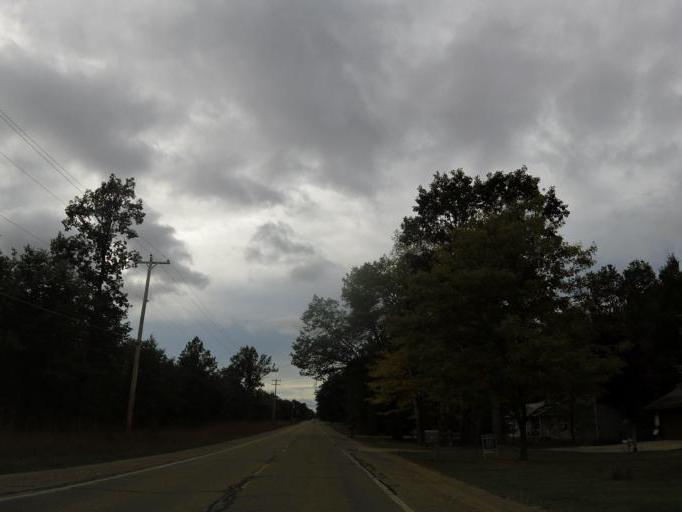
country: US
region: Michigan
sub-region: Roscommon County
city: Saint Helen
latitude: 44.3489
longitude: -84.4424
